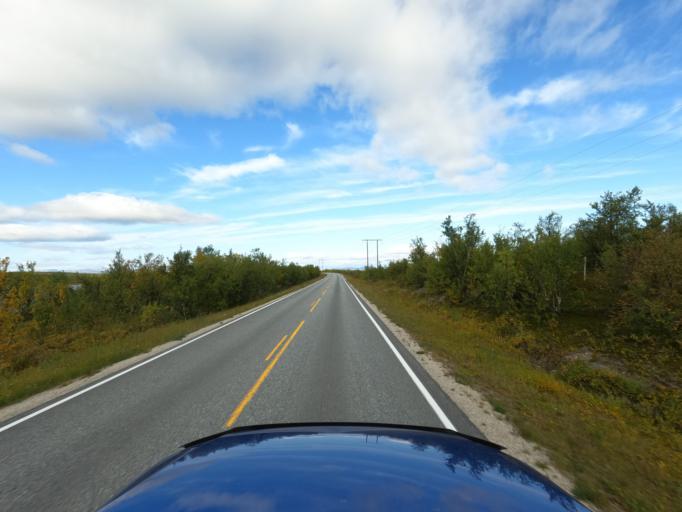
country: NO
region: Finnmark Fylke
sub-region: Karasjok
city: Karasjohka
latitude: 69.6624
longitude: 25.2764
